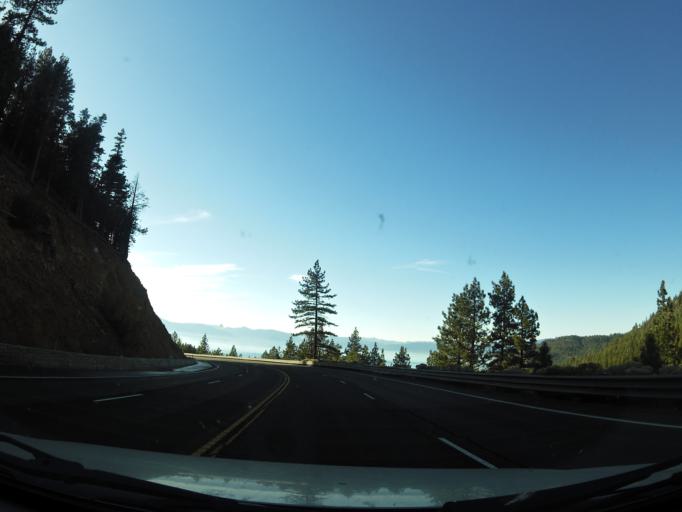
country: US
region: Nevada
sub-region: Douglas County
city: Kingsbury
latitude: 39.0855
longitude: -119.9262
